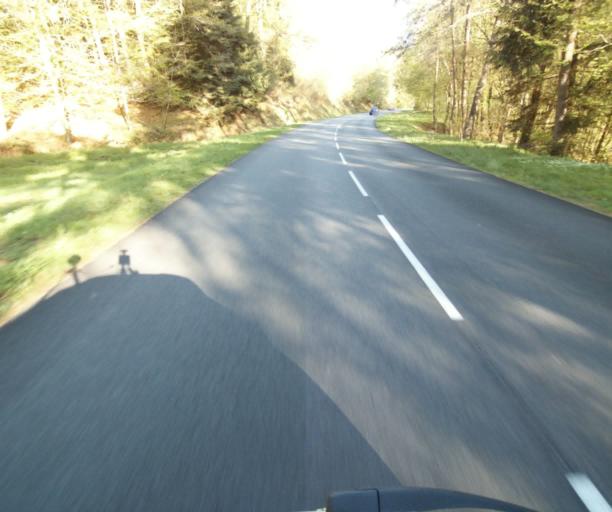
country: FR
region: Limousin
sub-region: Departement de la Correze
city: Correze
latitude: 45.3559
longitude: 1.8753
